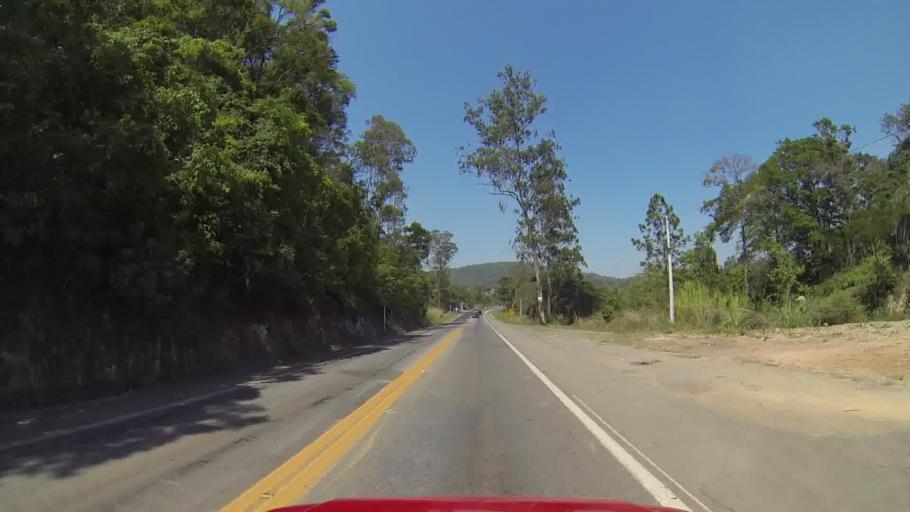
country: BR
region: Minas Gerais
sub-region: Mateus Leme
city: Mateus Leme
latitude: -20.0228
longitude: -44.5012
